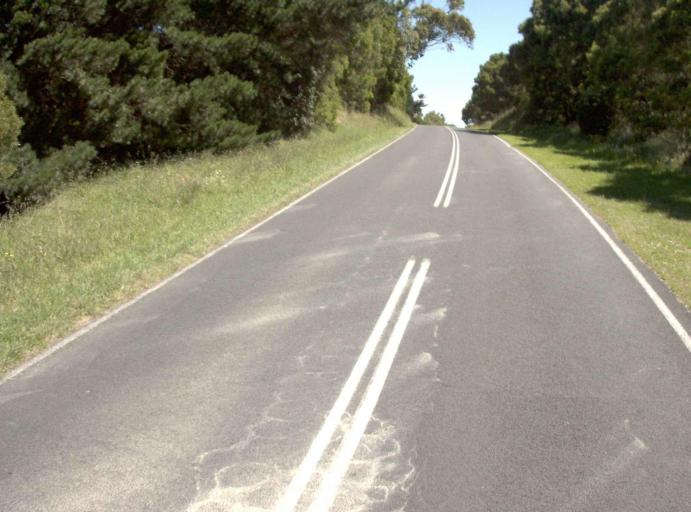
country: AU
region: Victoria
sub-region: Latrobe
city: Morwell
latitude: -38.6709
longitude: 146.1589
